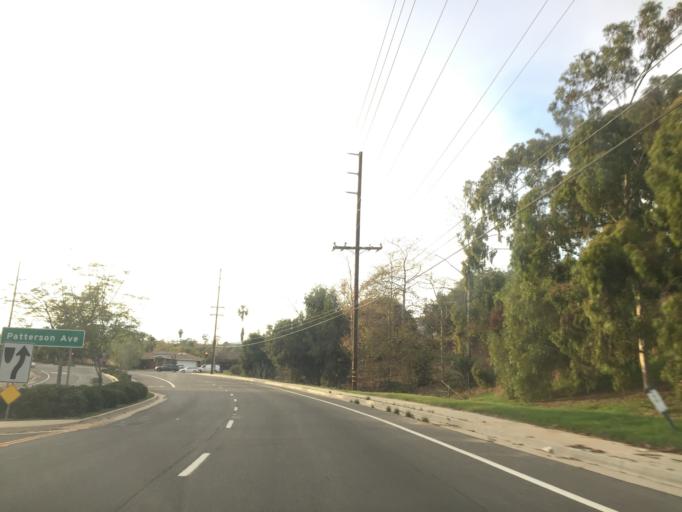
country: US
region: California
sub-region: Santa Barbara County
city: Goleta
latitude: 34.4529
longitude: -119.8064
